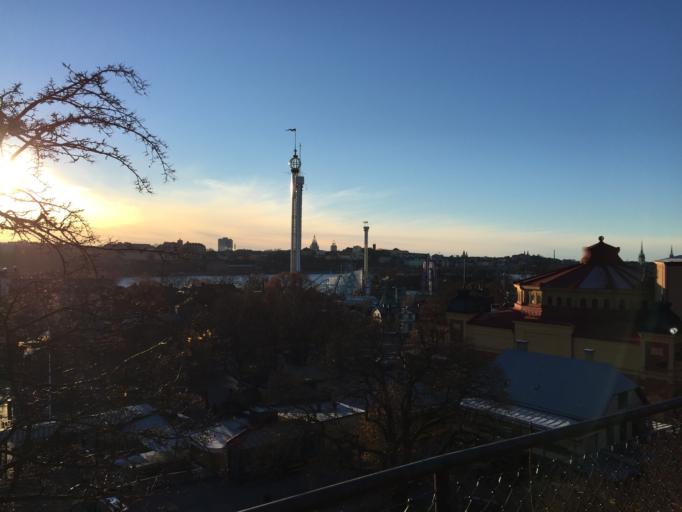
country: SE
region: Stockholm
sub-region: Stockholms Kommun
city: OEstermalm
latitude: 59.3250
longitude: 18.1019
